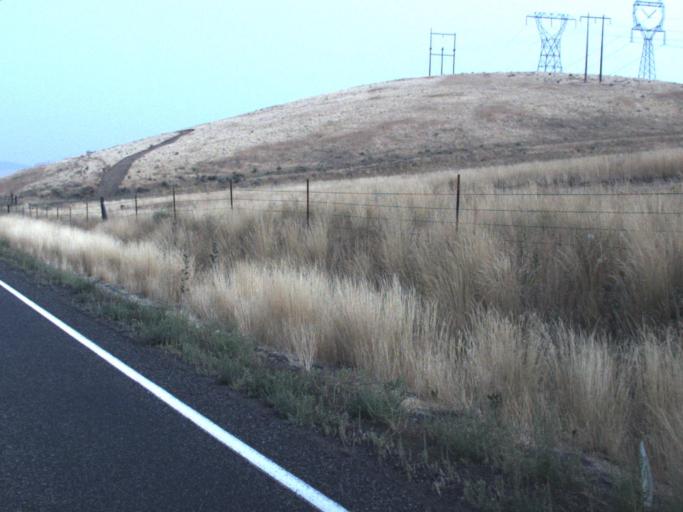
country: US
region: Washington
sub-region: Yakima County
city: Sunnyside
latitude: 46.4756
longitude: -119.9298
